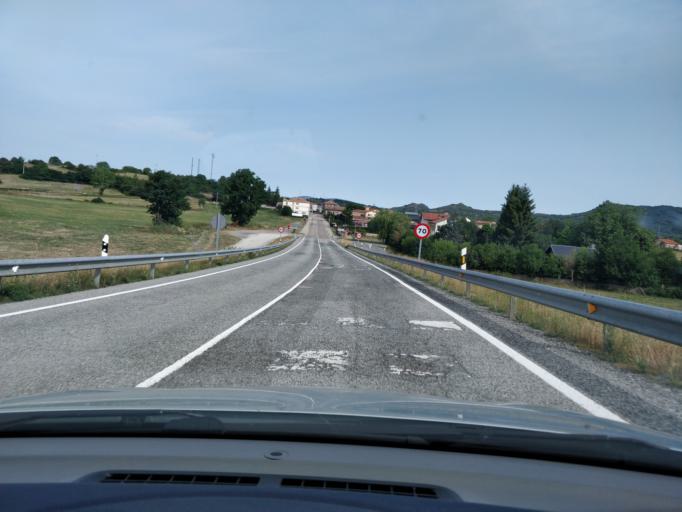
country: ES
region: Cantabria
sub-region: Provincia de Cantabria
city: San Pedro del Romeral
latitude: 42.9657
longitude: -3.7801
